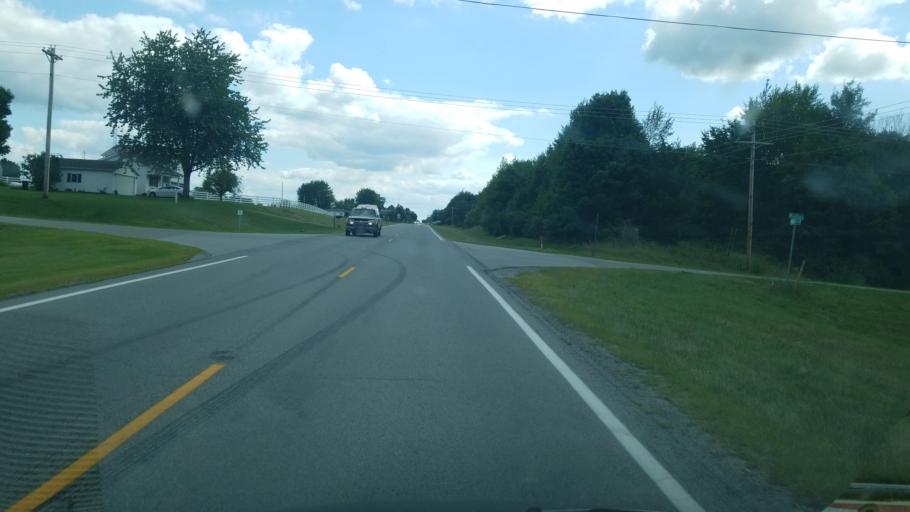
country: US
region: Ohio
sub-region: Allen County
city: Lima
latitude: 40.6593
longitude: -83.9756
